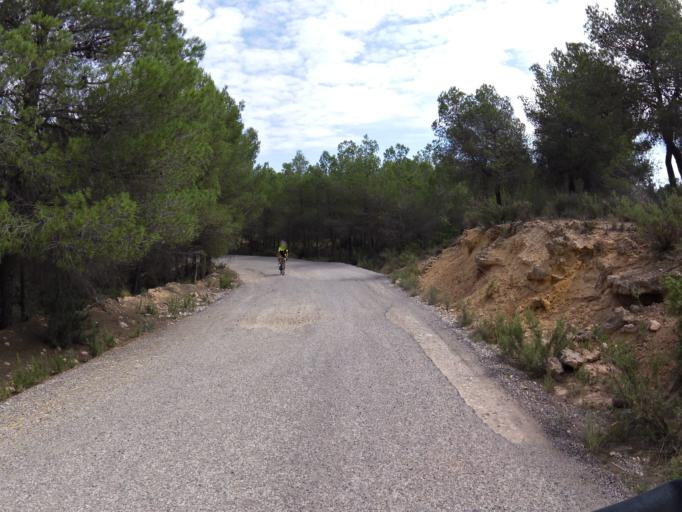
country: ES
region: Castille-La Mancha
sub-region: Provincia de Albacete
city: Casas Ibanez
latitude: 39.3571
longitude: -1.4722
